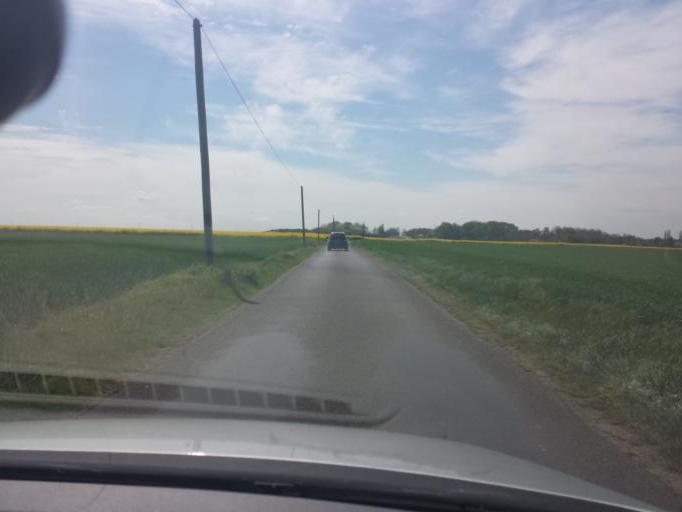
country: FR
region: Haute-Normandie
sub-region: Departement de l'Eure
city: Breteuil
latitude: 48.8058
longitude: 0.9672
